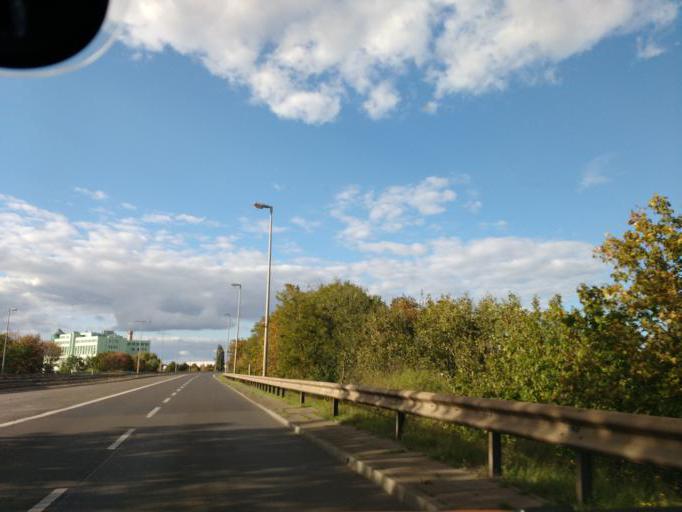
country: DE
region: Berlin
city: Tempelhof Bezirk
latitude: 52.4539
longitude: 13.4149
